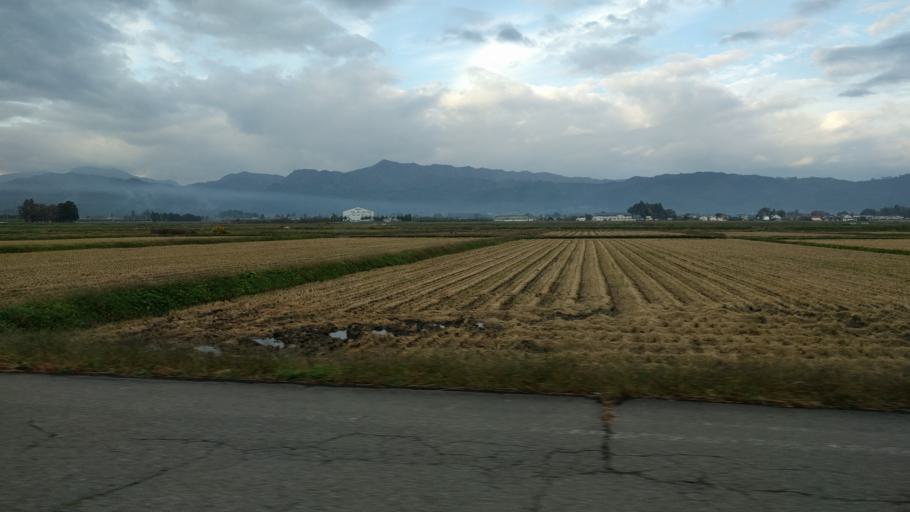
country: JP
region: Fukushima
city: Kitakata
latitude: 37.4507
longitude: 139.8554
